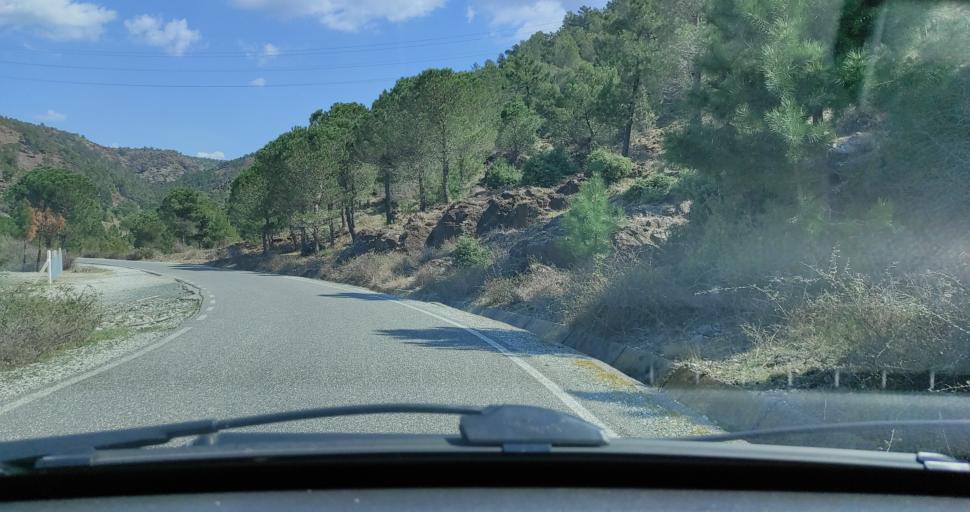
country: AL
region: Shkoder
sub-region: Rrethi i Shkodres
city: Vau i Dejes
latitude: 41.9876
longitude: 19.6443
